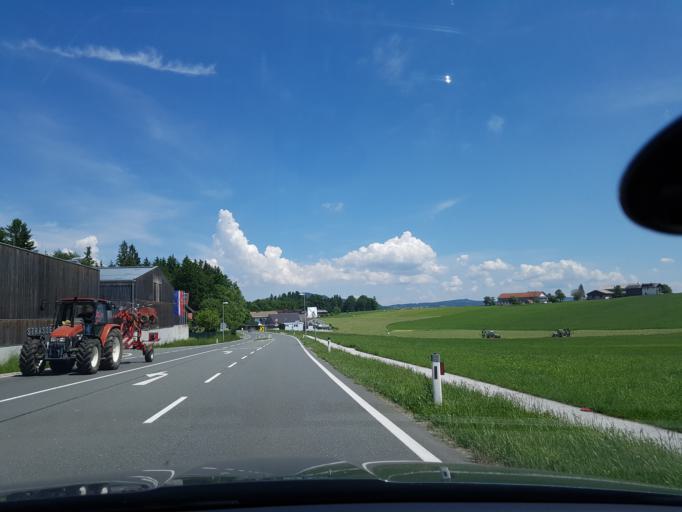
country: AT
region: Salzburg
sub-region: Politischer Bezirk Salzburg-Umgebung
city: Obertrum am See
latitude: 47.9065
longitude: 13.0805
